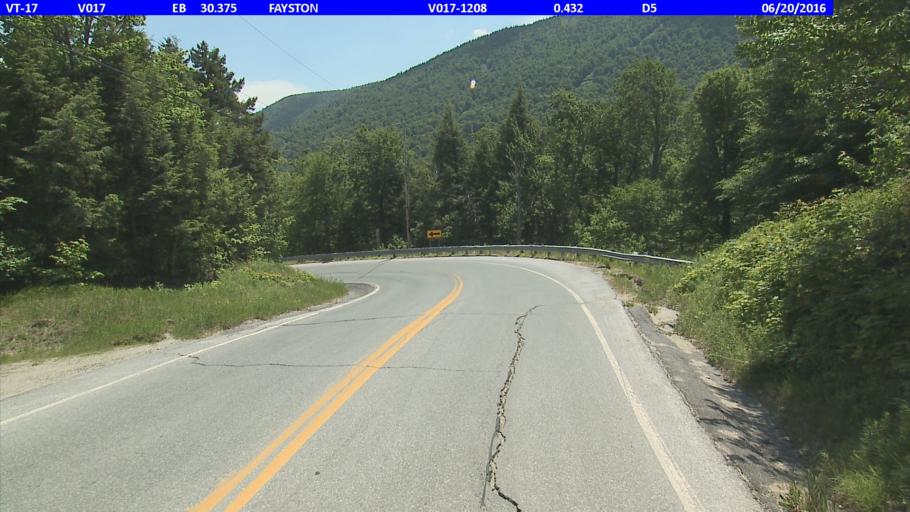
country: US
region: Vermont
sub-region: Addison County
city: Bristol
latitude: 44.2053
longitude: -72.9223
